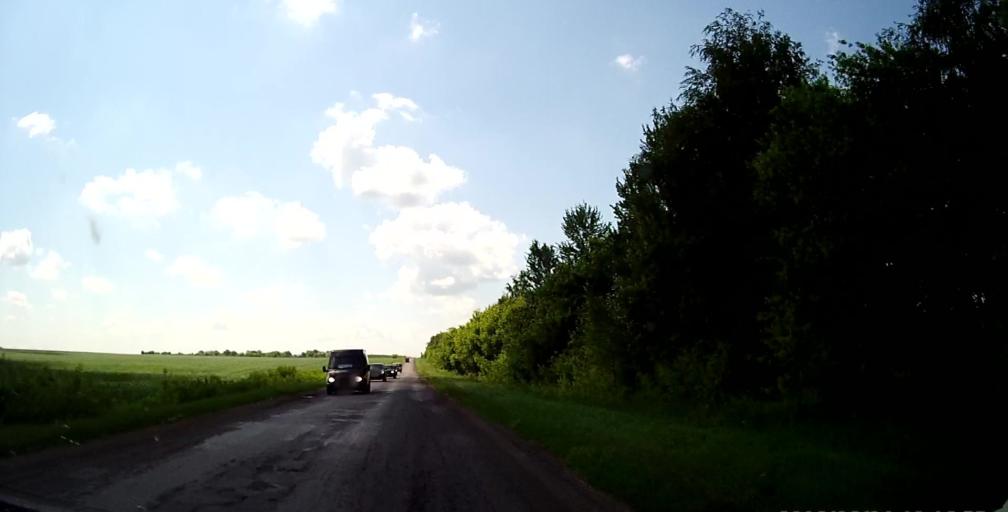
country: RU
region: Lipetsk
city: Chaplygin
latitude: 53.2815
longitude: 39.9615
